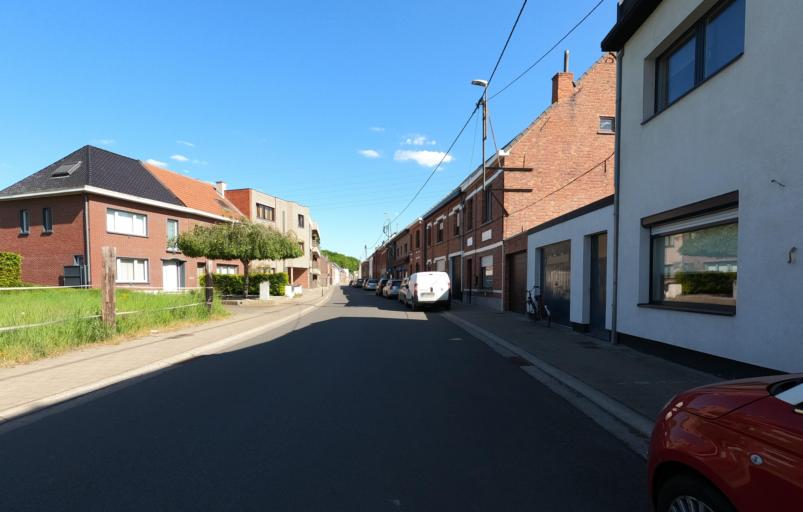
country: BE
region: Flanders
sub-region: Provincie Oost-Vlaanderen
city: Lebbeke
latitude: 50.9961
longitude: 4.1439
